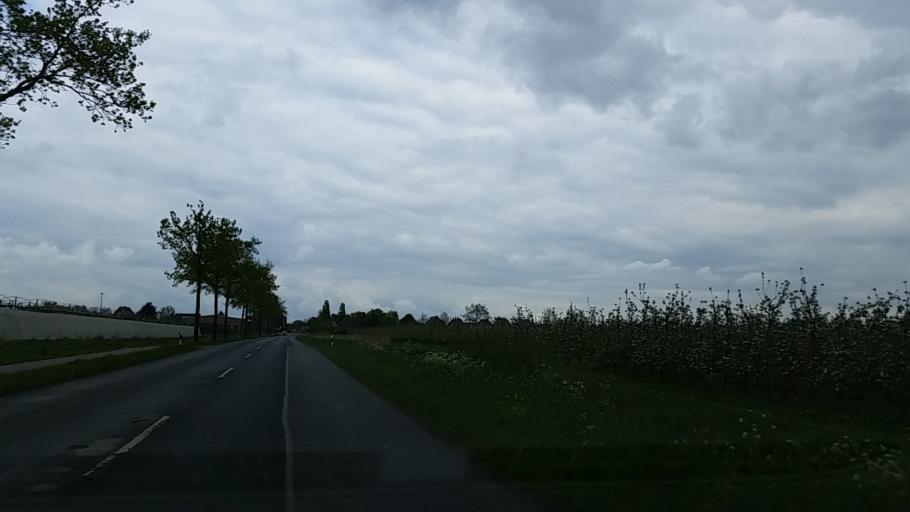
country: DE
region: Lower Saxony
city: Jork
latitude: 53.5148
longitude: 9.6687
